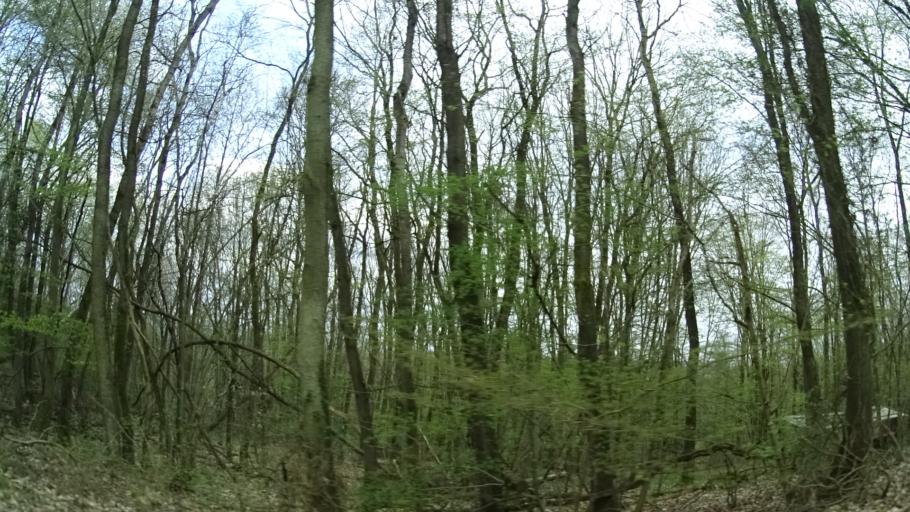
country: DE
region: Rheinland-Pfalz
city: Heinzenberg
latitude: 49.8185
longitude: 7.4752
